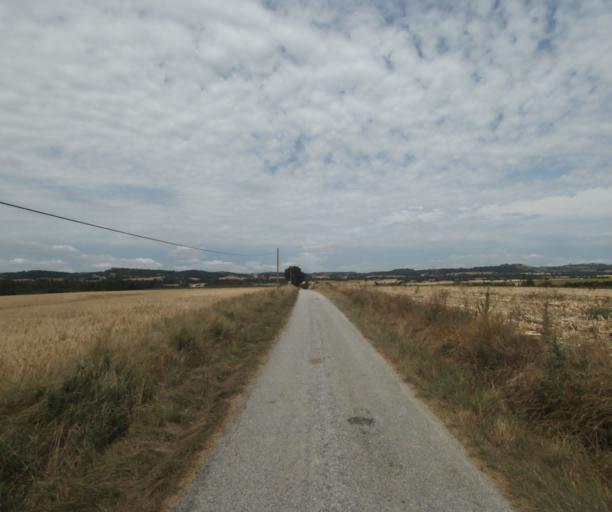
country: FR
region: Midi-Pyrenees
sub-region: Departement de la Haute-Garonne
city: Saint-Felix-Lauragais
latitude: 43.4033
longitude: 1.9028
